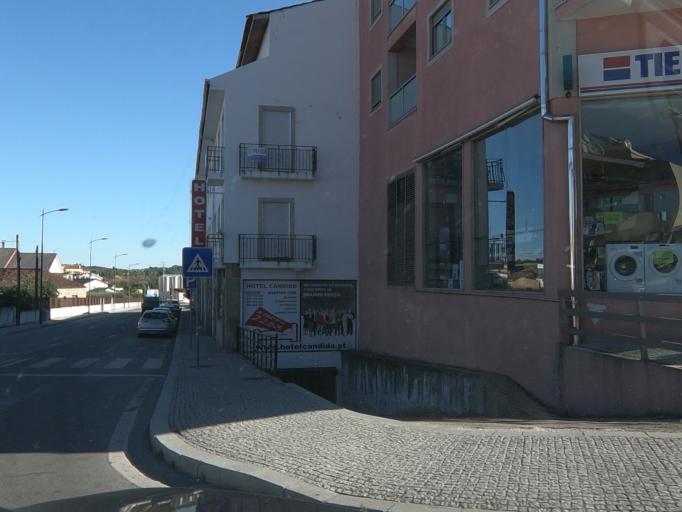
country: PT
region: Vila Real
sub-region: Valpacos
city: Valpacos
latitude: 41.6044
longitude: -7.3106
